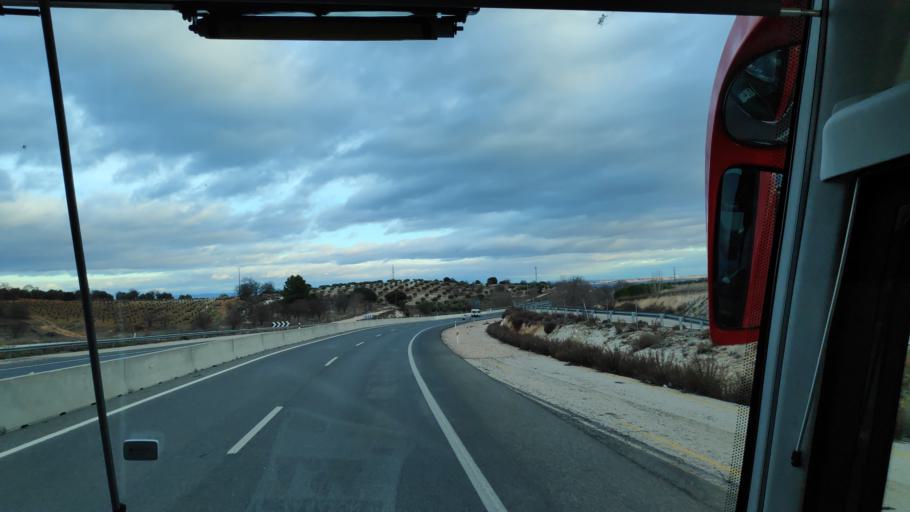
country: ES
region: Madrid
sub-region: Provincia de Madrid
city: Villarejo de Salvanes
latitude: 40.1564
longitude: -3.2557
